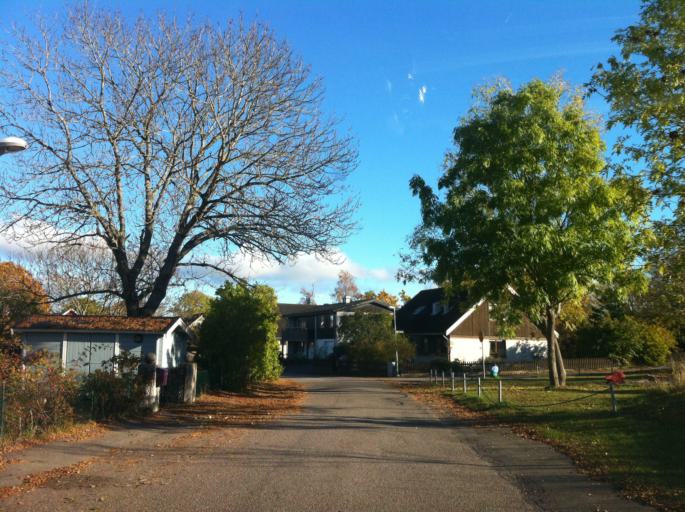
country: SE
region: Uppsala
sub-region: Osthammars Kommun
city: Oregrund
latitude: 60.3368
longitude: 18.4408
